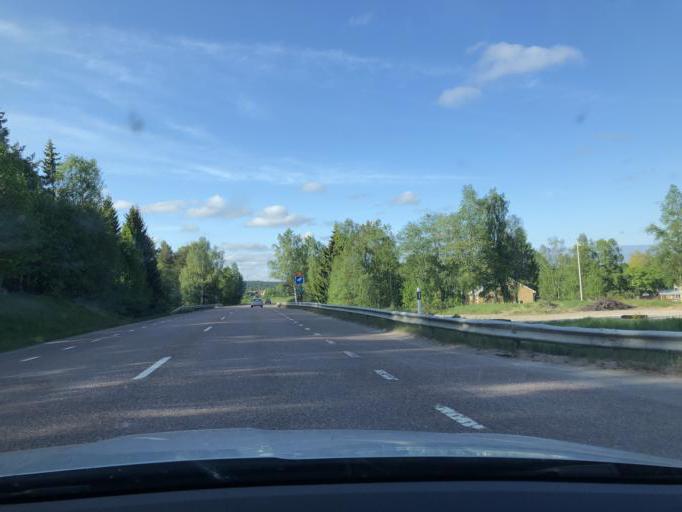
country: SE
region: Gaevleborg
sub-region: Nordanstigs Kommun
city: Bergsjoe
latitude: 61.9236
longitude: 17.2132
